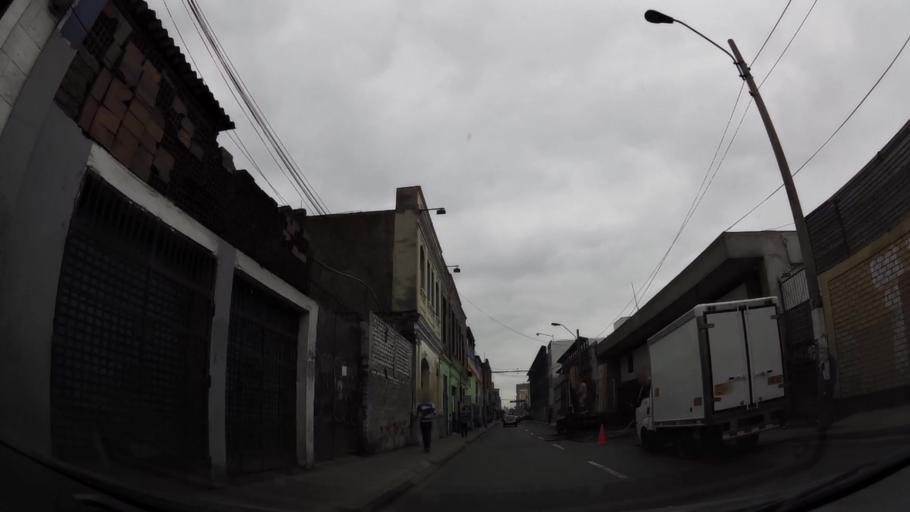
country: PE
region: Lima
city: Lima
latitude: -12.0532
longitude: -77.0407
